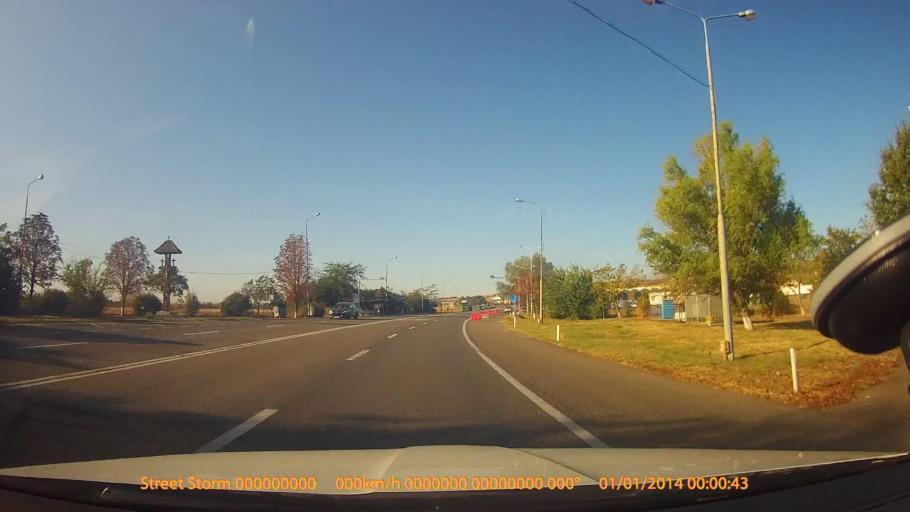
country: RO
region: Vaslui
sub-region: Comuna Dranceni
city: Rasesti
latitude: 46.7841
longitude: 28.1365
